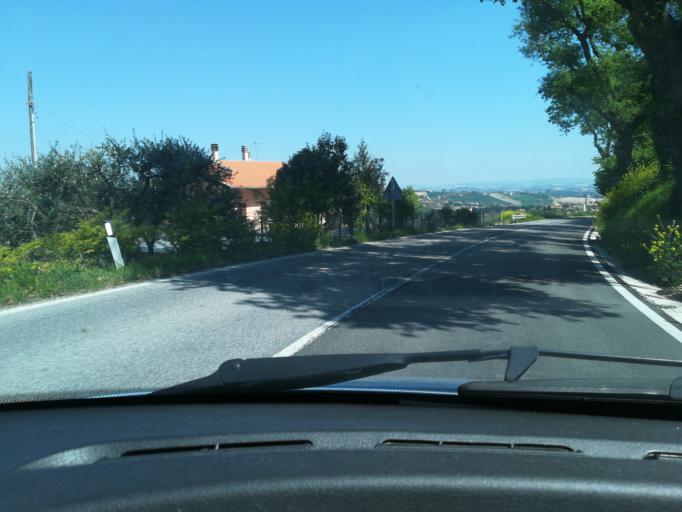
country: IT
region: The Marches
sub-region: Provincia di Macerata
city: Cingoli
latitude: 43.3912
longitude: 13.2067
